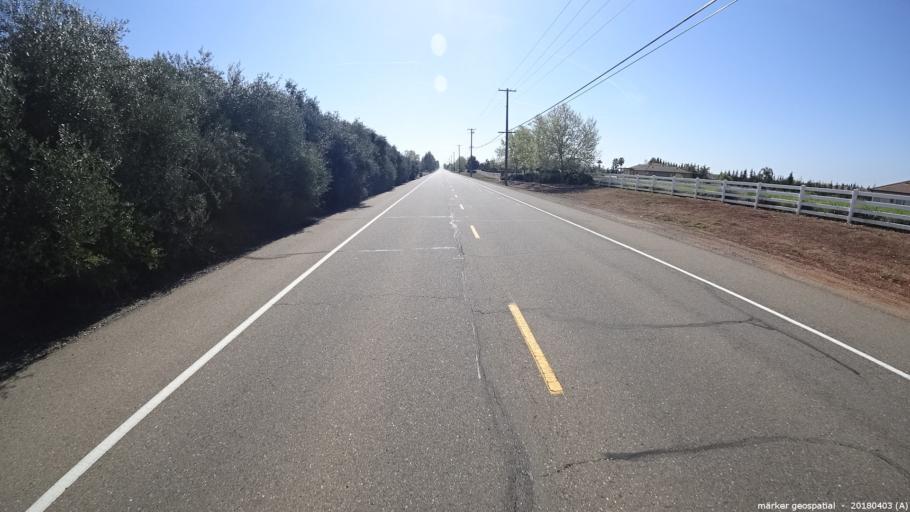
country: US
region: California
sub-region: Sacramento County
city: Wilton
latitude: 38.4228
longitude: -121.1917
